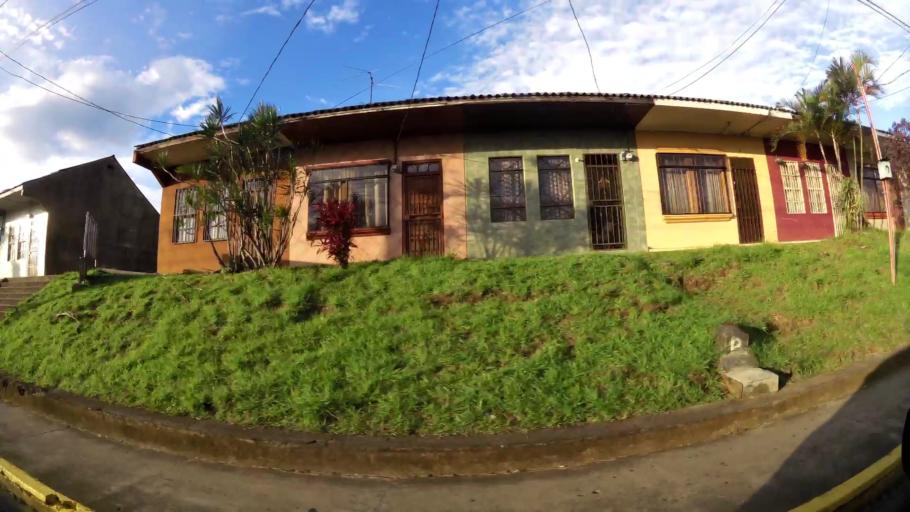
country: CR
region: Heredia
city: San Francisco
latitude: 9.9969
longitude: -84.1229
